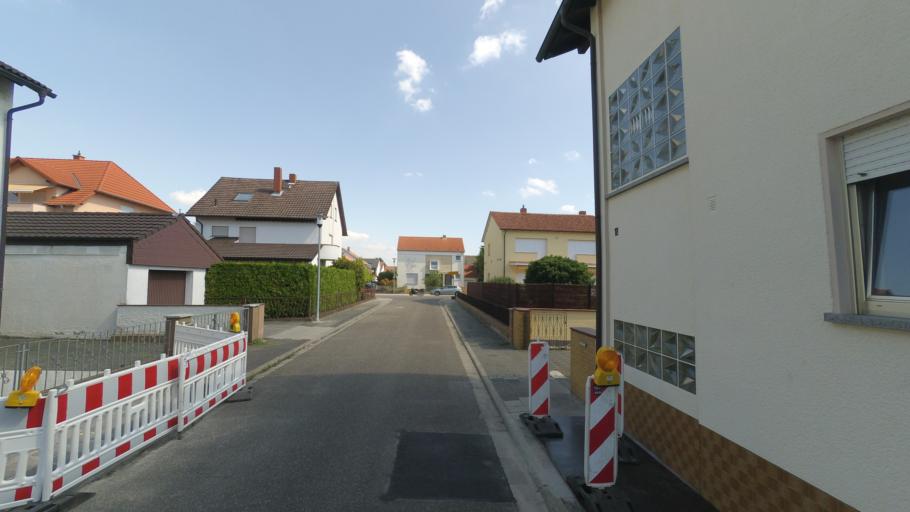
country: DE
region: Rheinland-Pfalz
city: Schifferstadt
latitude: 49.3804
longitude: 8.3814
